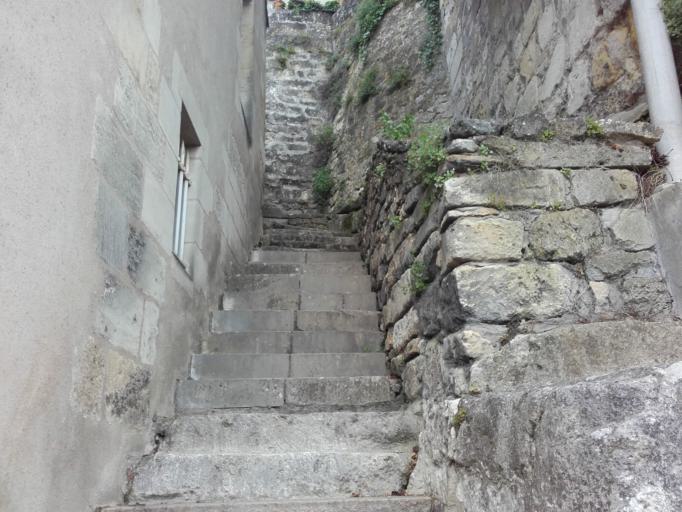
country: FR
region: Aquitaine
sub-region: Departement de la Gironde
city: Saint-Emilion
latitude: 44.8923
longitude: -0.1548
